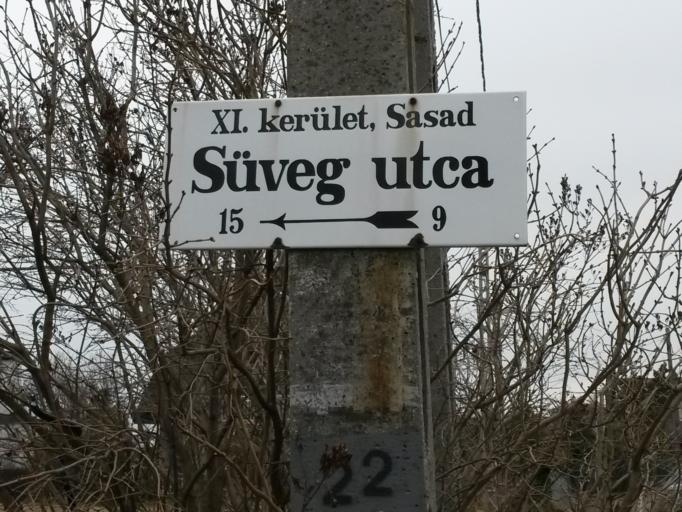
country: HU
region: Budapest
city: Budapest XII. keruelet
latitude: 47.4814
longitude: 19.0078
